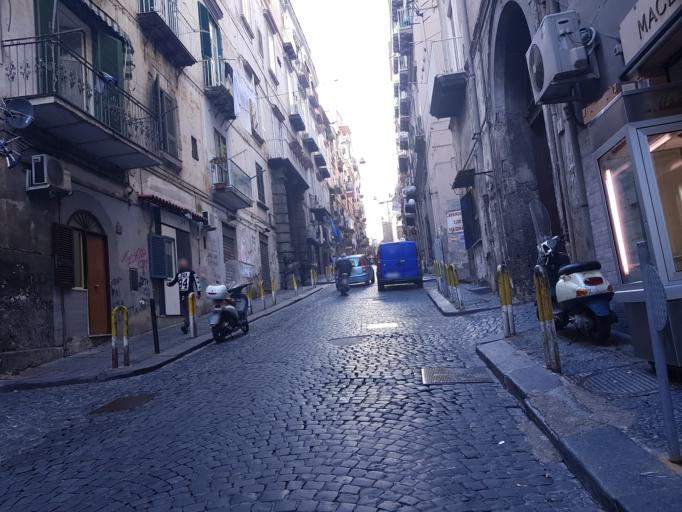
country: IT
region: Campania
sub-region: Provincia di Napoli
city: Napoli
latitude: 40.8442
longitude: 14.2463
